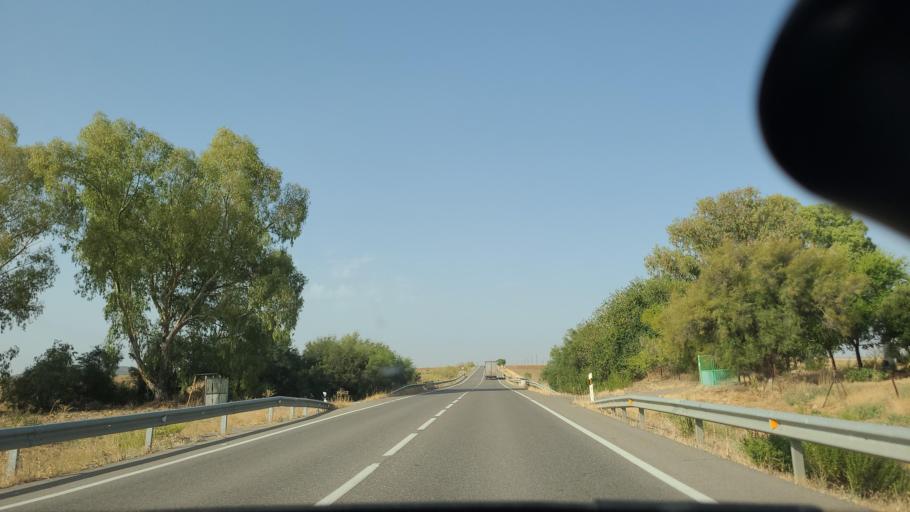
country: ES
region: Andalusia
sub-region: Province of Cordoba
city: Fuente Obejuna
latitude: 38.2940
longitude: -5.3488
